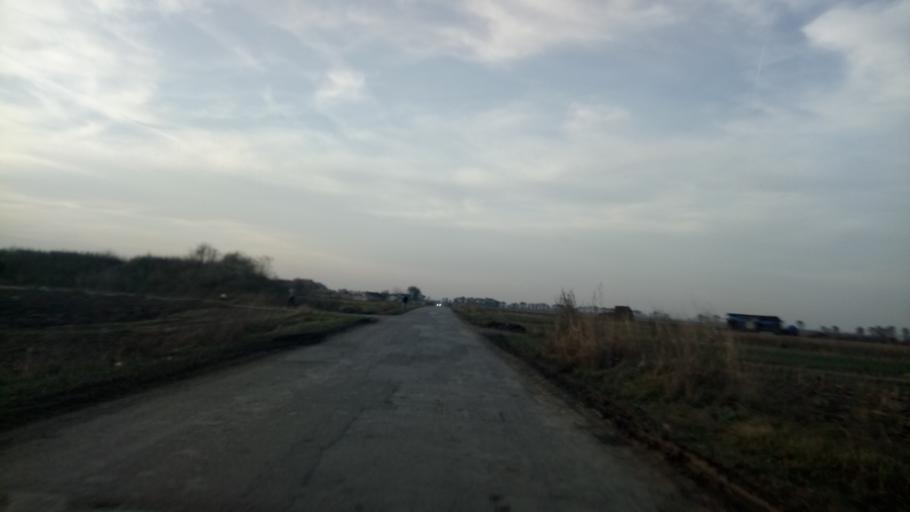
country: RS
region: Autonomna Pokrajina Vojvodina
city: Nova Pazova
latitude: 44.9551
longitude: 20.2241
